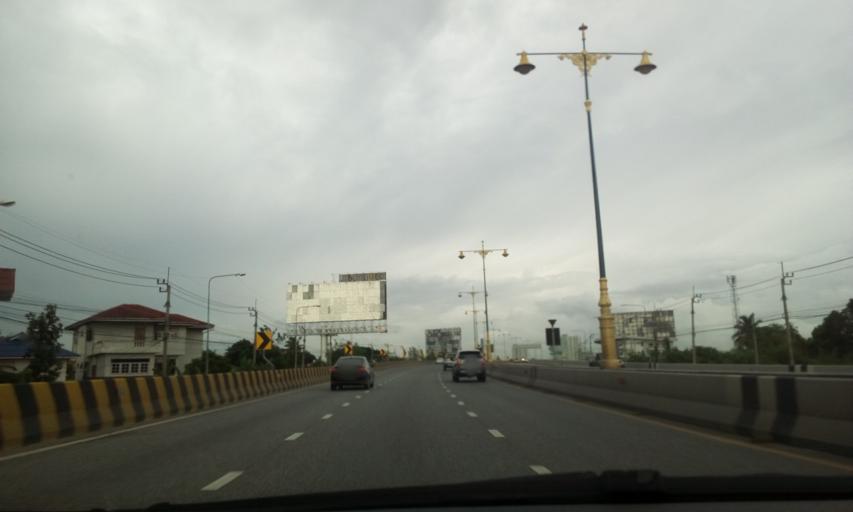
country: TH
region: Nonthaburi
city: Pak Kret
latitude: 13.9201
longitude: 100.4893
